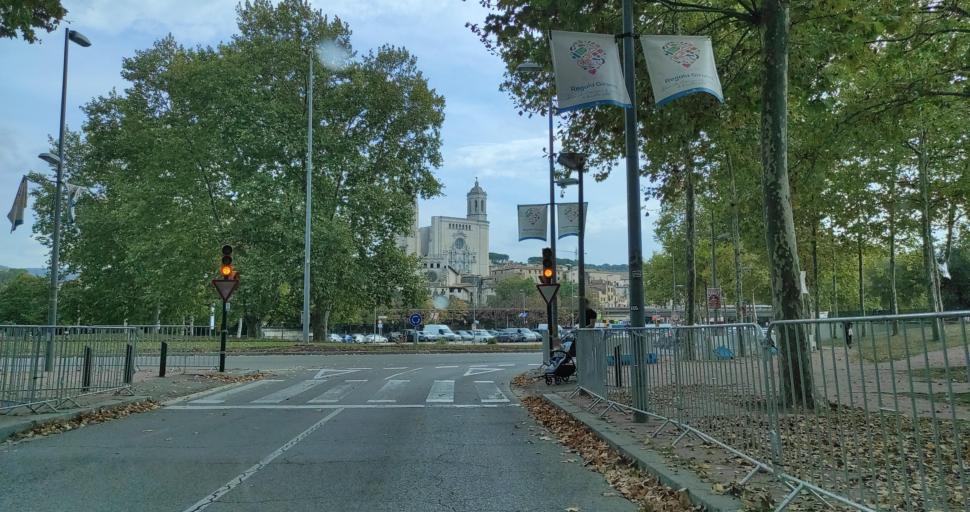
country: ES
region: Catalonia
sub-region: Provincia de Girona
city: Girona
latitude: 41.9894
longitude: 2.8215
